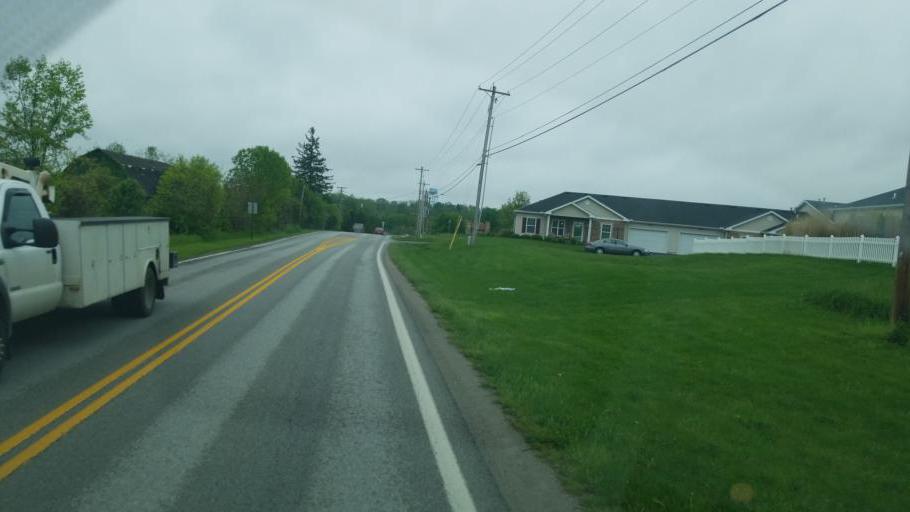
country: US
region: Ohio
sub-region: Highland County
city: Hillsboro
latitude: 39.2203
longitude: -83.6190
